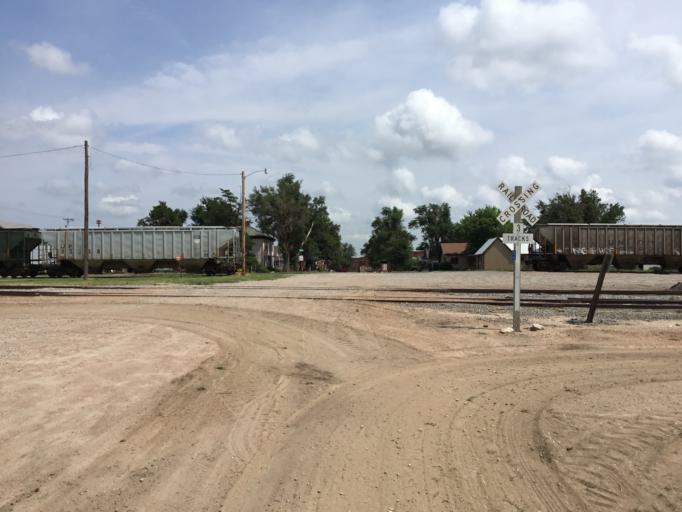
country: US
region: Kansas
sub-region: Pratt County
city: Pratt
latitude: 37.4971
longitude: -98.6825
